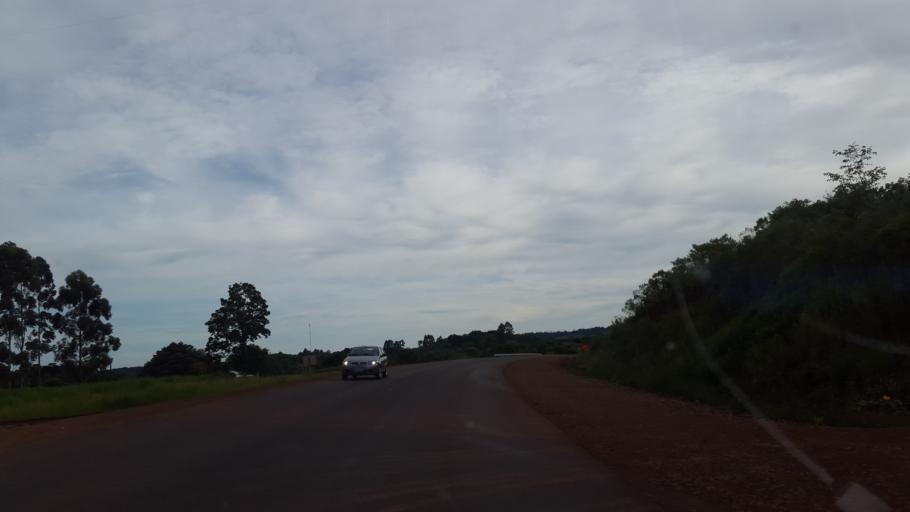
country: AR
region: Misiones
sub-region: Departamento de San Pedro
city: San Pedro
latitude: -26.4853
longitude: -53.8889
